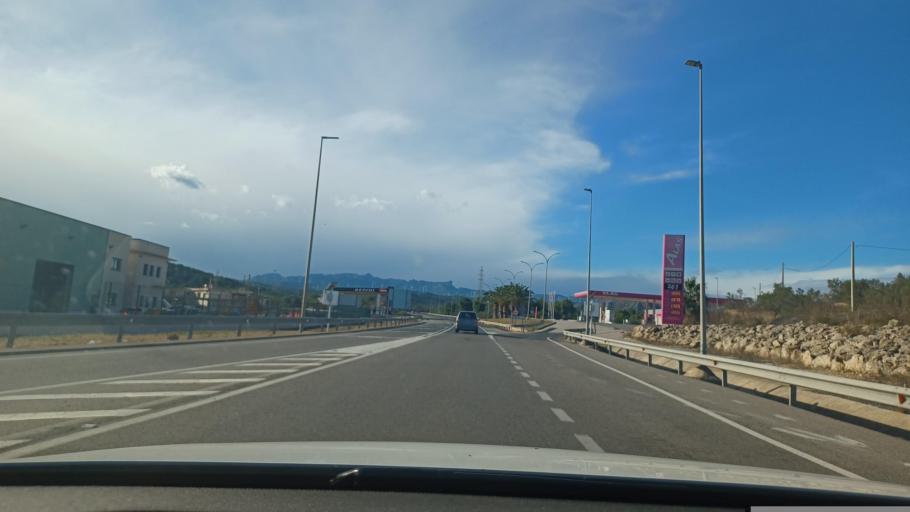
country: ES
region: Catalonia
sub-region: Provincia de Tarragona
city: El Perello
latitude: 40.8968
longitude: 0.7503
